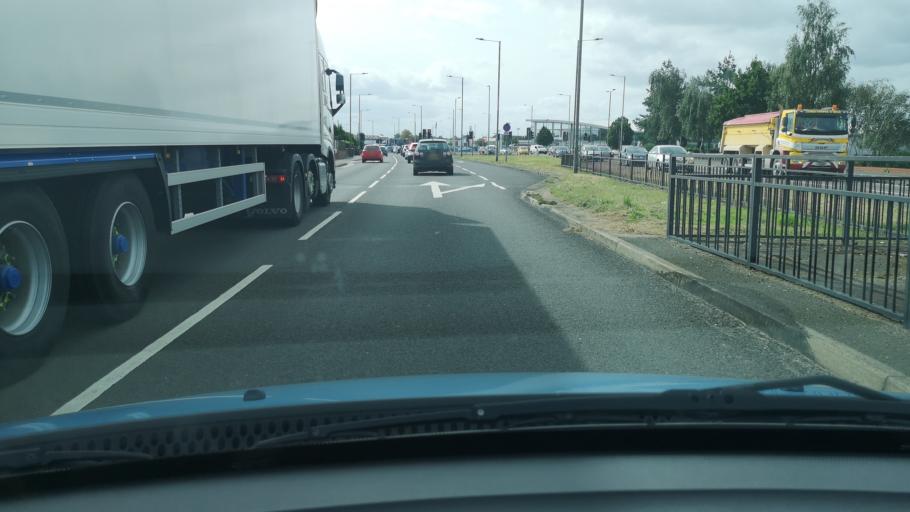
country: GB
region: England
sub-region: Doncaster
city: Doncaster
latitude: 53.5377
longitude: -1.1186
